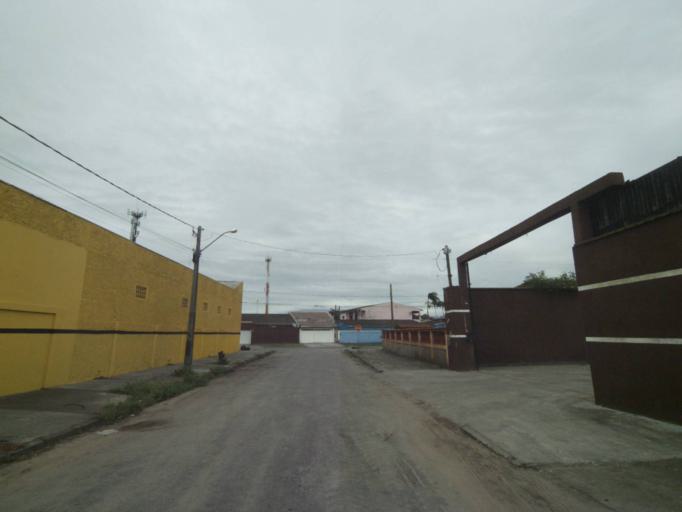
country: BR
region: Parana
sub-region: Paranagua
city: Paranagua
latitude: -25.5168
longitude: -48.5337
